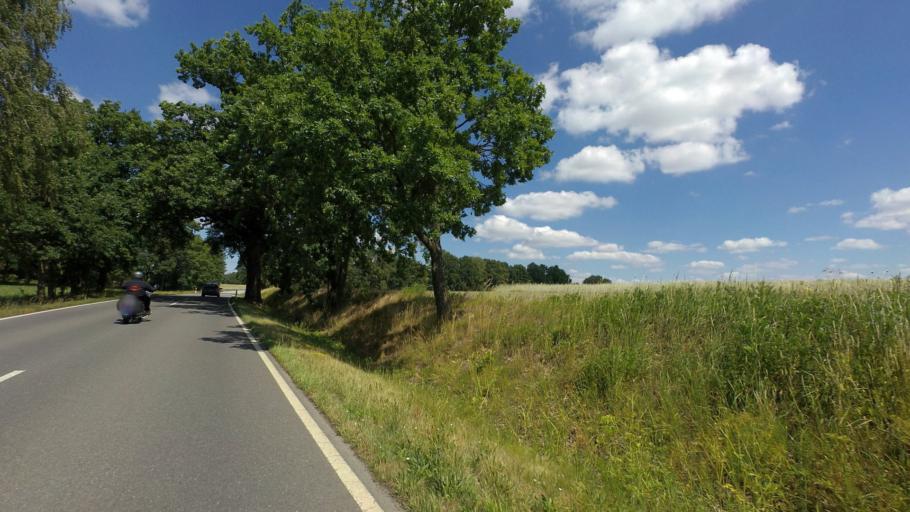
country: DE
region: Brandenburg
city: Luckau
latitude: 51.8118
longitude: 13.6774
